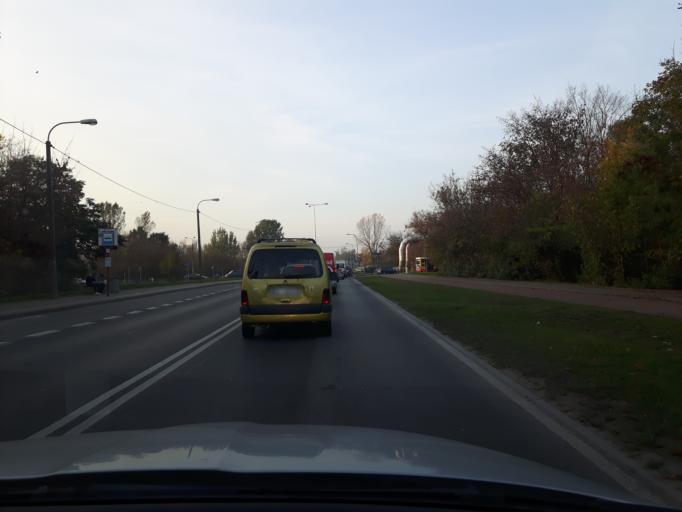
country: PL
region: Masovian Voivodeship
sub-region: Warszawa
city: Praga Poludnie
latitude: 52.2670
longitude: 21.0739
